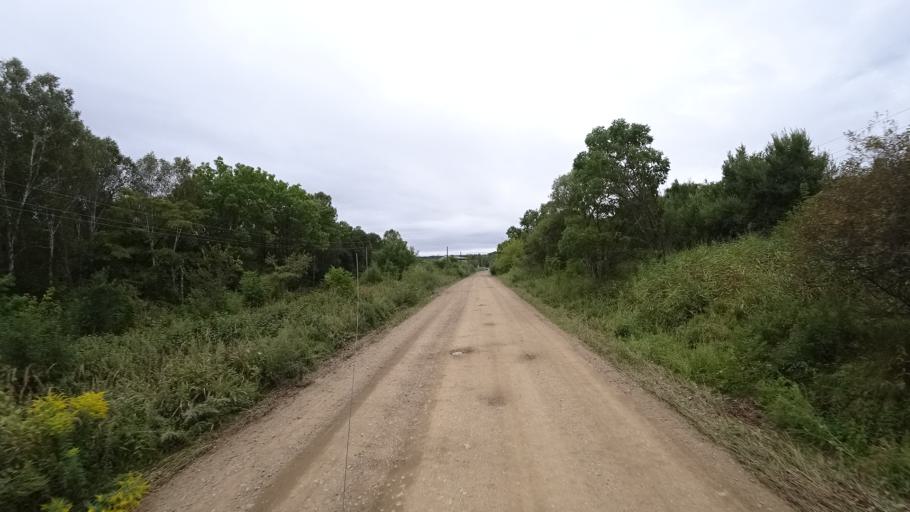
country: RU
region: Primorskiy
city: Rettikhovka
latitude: 44.1693
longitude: 132.7822
